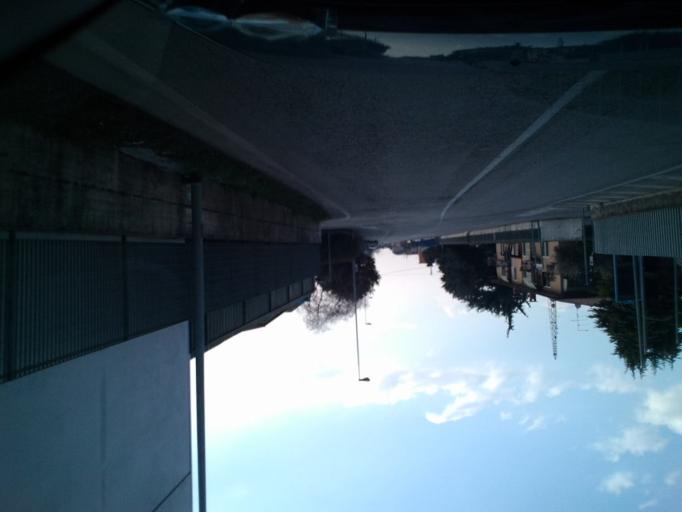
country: IT
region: Veneto
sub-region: Provincia di Verona
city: Villafranca di Verona
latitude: 45.3709
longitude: 10.8630
